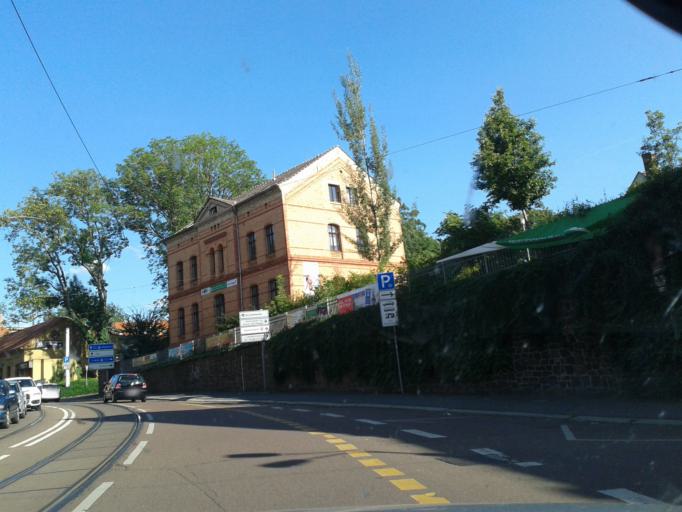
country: DE
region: Saxony-Anhalt
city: Sennewitz
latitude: 51.5024
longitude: 11.9532
